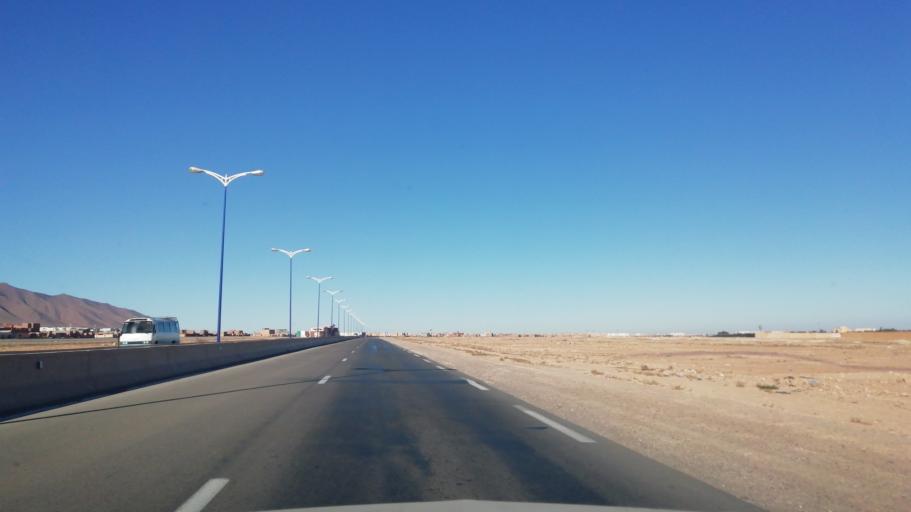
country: DZ
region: Wilaya de Naama
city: Naama
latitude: 33.5236
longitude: -0.2748
